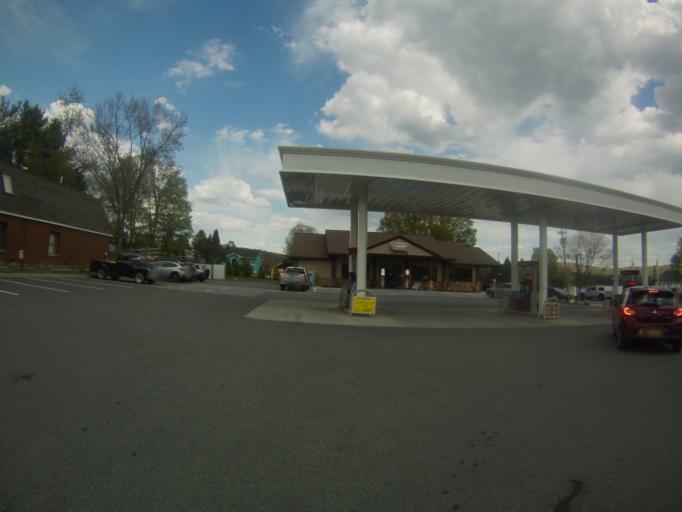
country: US
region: New York
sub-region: Essex County
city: Ticonderoga
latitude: 43.8357
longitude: -73.7620
